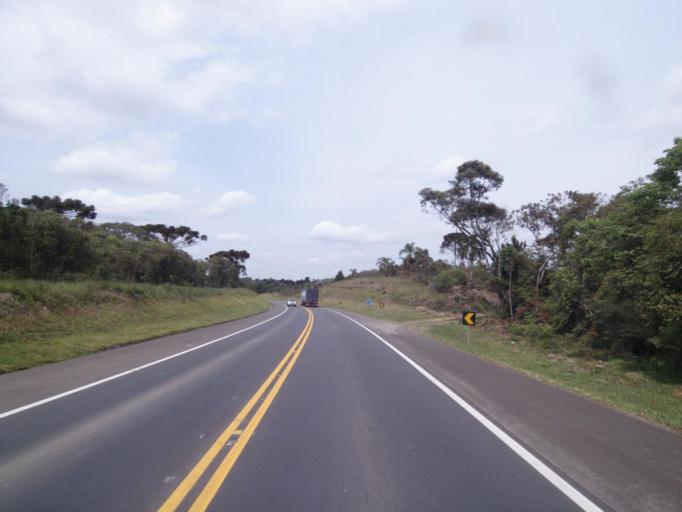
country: BR
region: Parana
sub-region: Irati
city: Irati
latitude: -25.4729
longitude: -50.4893
